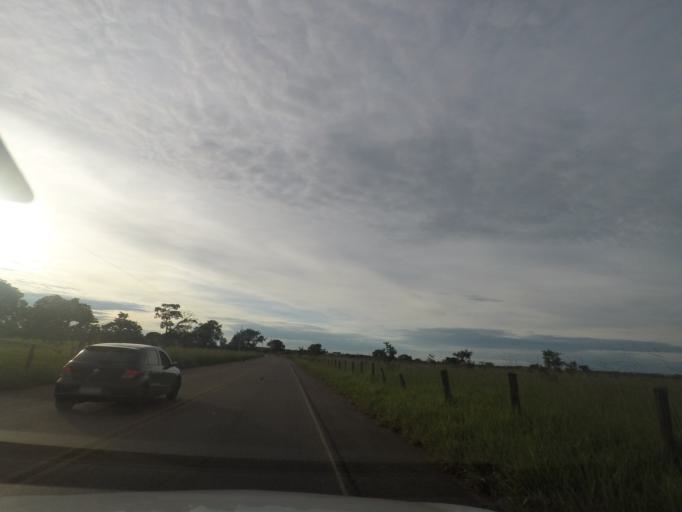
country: BR
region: Goias
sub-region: Trindade
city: Trindade
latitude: -16.7317
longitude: -49.4235
